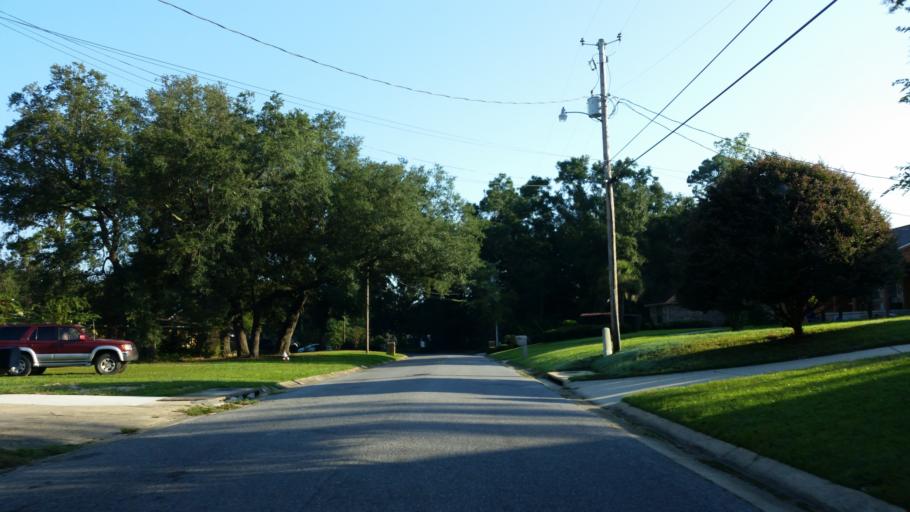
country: US
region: Florida
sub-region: Escambia County
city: Ferry Pass
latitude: 30.5427
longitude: -87.2275
